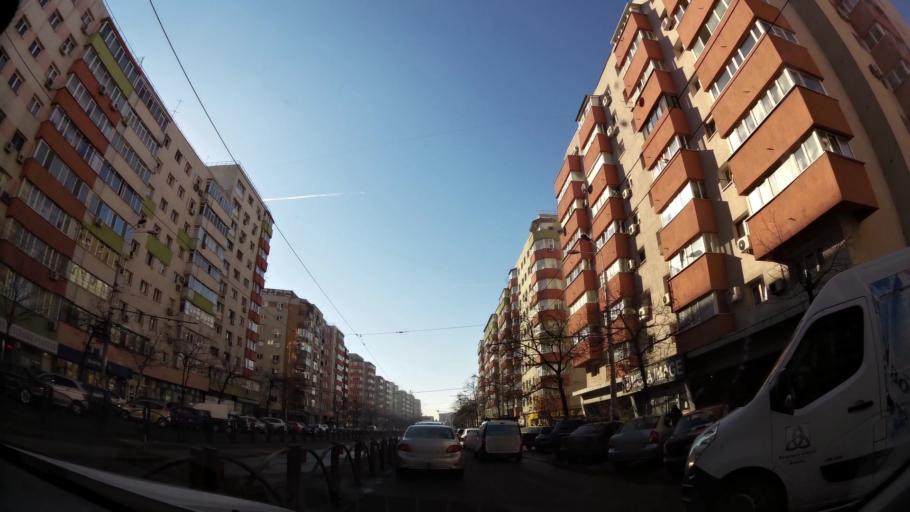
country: RO
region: Bucuresti
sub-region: Municipiul Bucuresti
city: Bucharest
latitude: 44.4419
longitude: 26.1178
